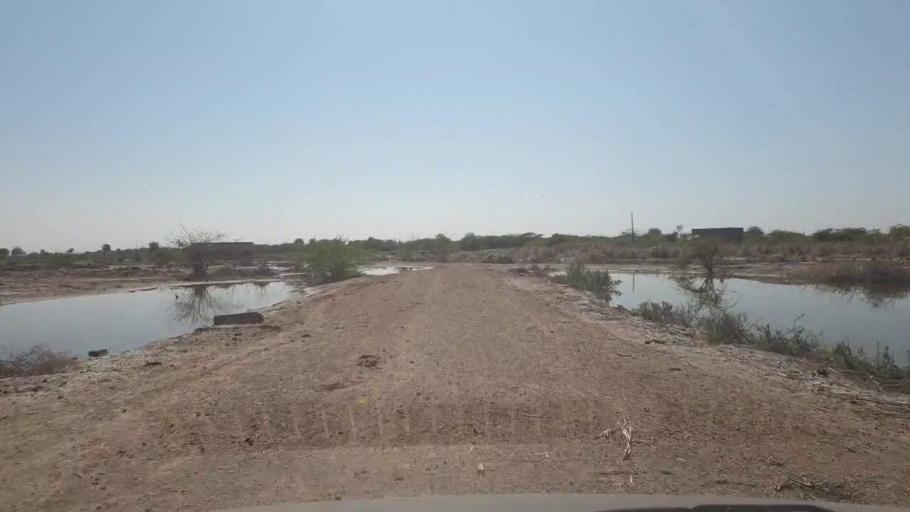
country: PK
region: Sindh
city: Dhoro Naro
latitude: 25.4438
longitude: 69.6100
